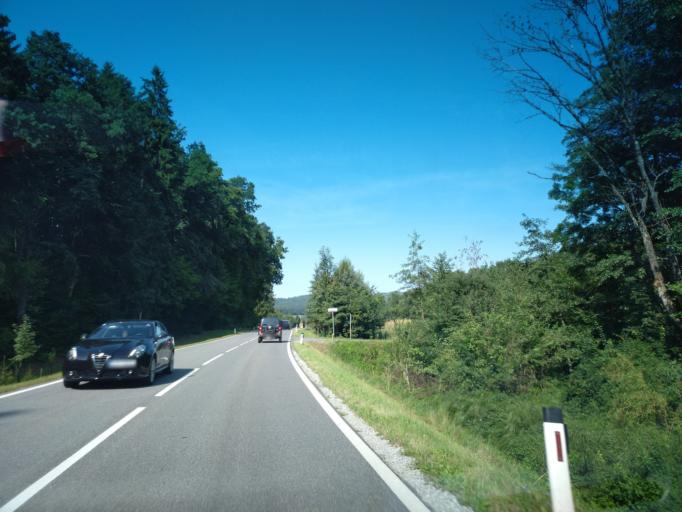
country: AT
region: Styria
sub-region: Politischer Bezirk Leibnitz
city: Heimschuh
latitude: 46.7483
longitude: 15.4730
